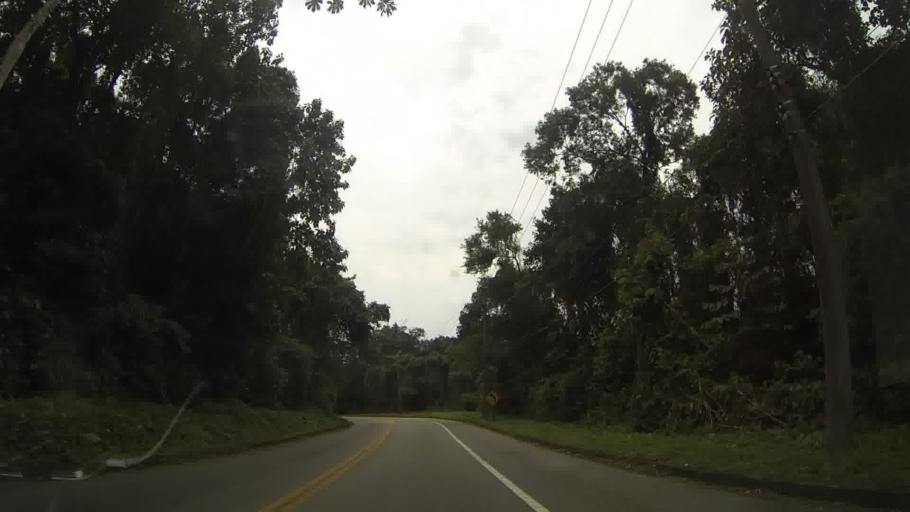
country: BR
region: Sao Paulo
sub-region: Sao Sebastiao
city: Sao Sebastiao
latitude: -23.8144
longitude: -45.4675
